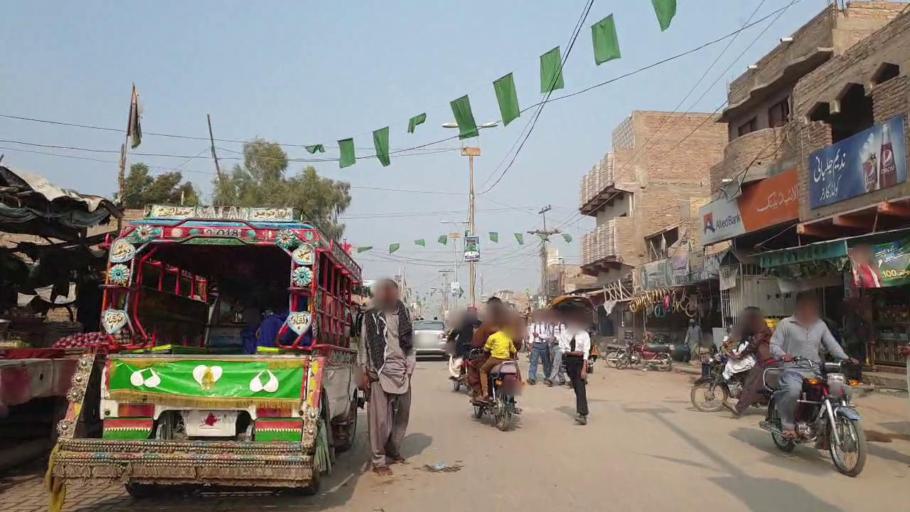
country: PK
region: Sindh
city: Bhan
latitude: 26.5596
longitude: 67.7214
